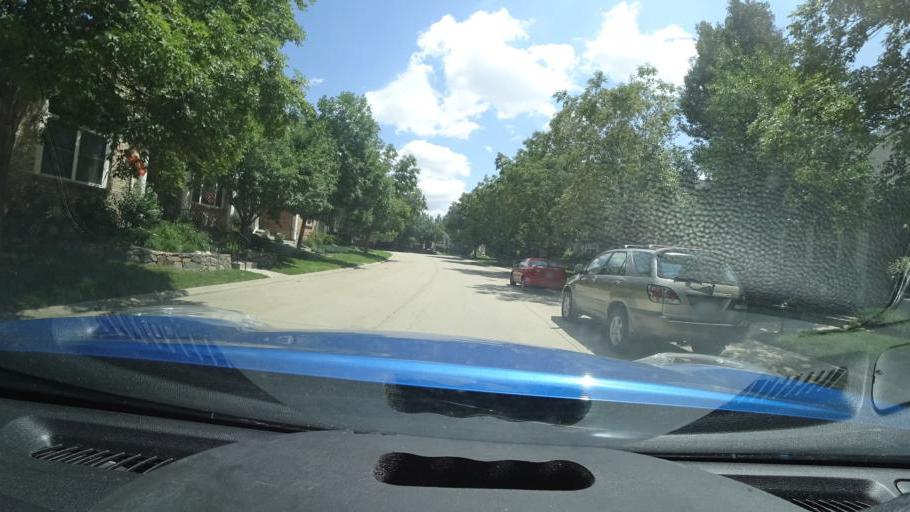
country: US
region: Colorado
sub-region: Arapahoe County
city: Glendale
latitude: 39.6989
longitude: -104.8969
